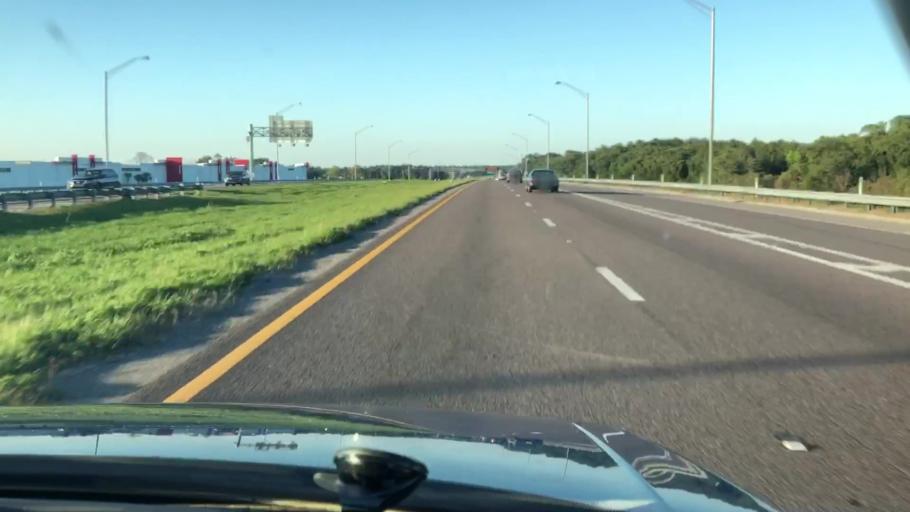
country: US
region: Florida
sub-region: Orange County
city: Ocoee
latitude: 28.5777
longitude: -81.5570
